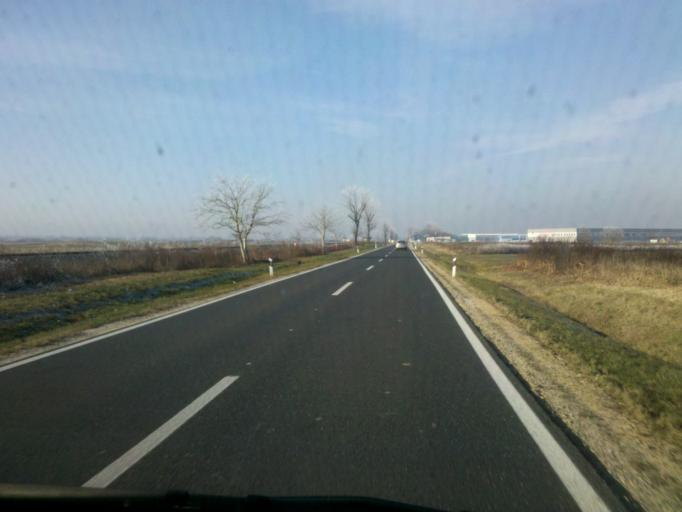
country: HR
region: Koprivnicko-Krizevacka
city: Kalinovac
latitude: 46.0091
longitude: 17.1022
